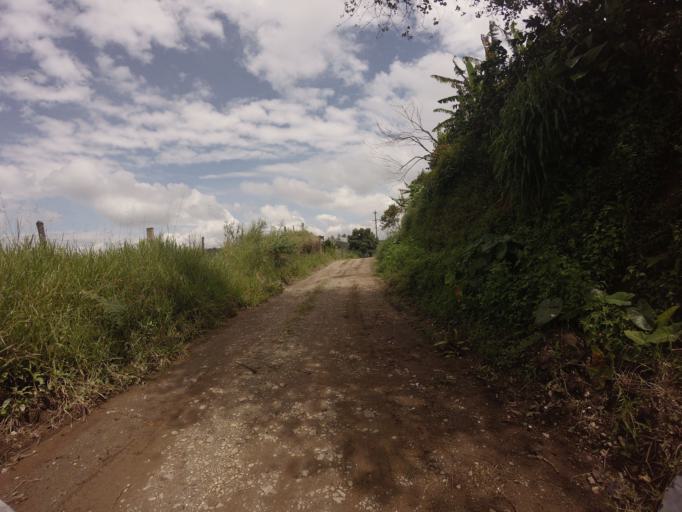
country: CO
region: Valle del Cauca
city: Ulloa
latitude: 4.7081
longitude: -75.7179
